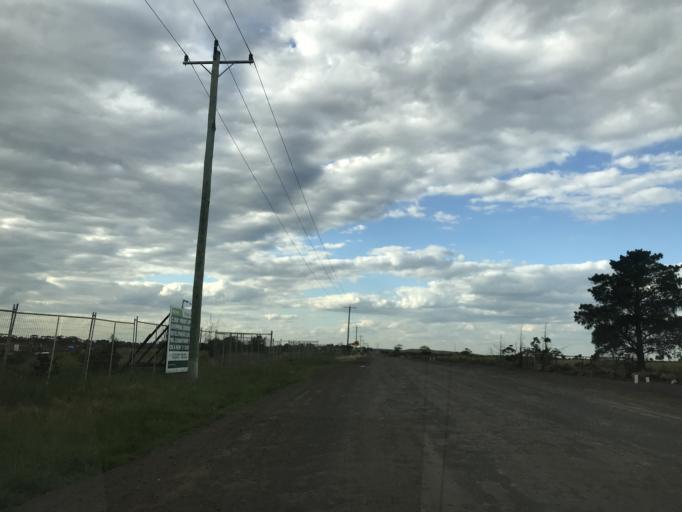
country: AU
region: Victoria
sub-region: Wyndham
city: Truganina
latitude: -37.8207
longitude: 144.7217
